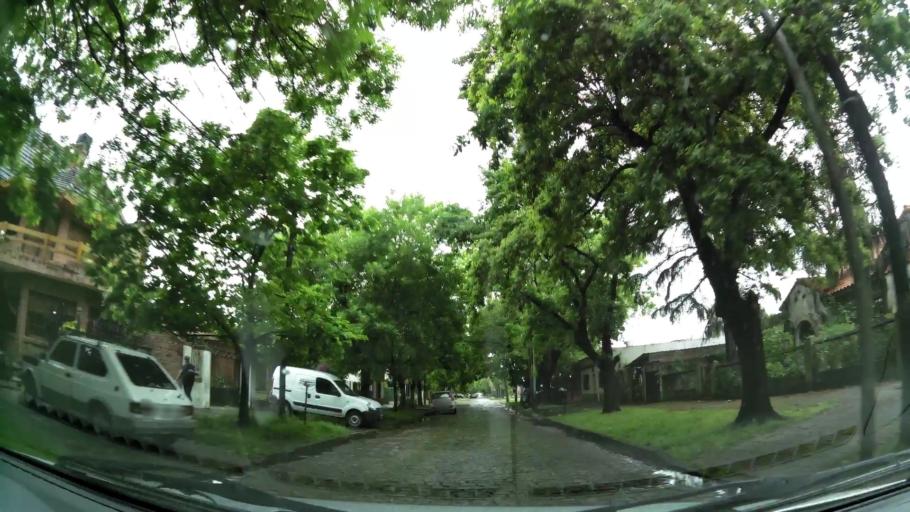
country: AR
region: Buenos Aires
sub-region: Partido de Lomas de Zamora
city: Lomas de Zamora
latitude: -34.7503
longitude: -58.3914
